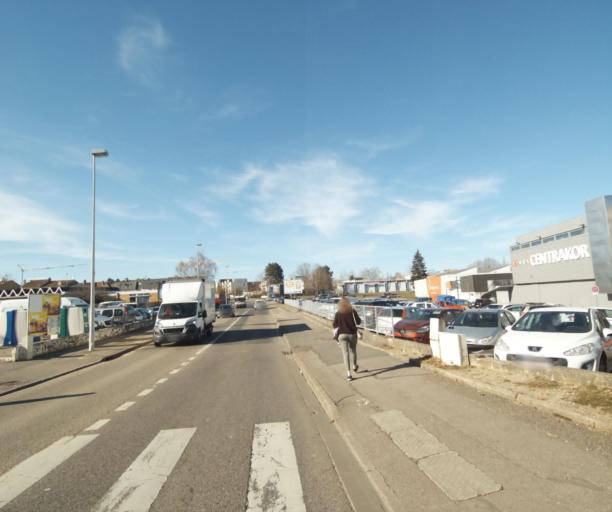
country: FR
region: Lorraine
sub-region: Departement de Meurthe-et-Moselle
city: Nancy
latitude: 48.6674
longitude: 6.1885
